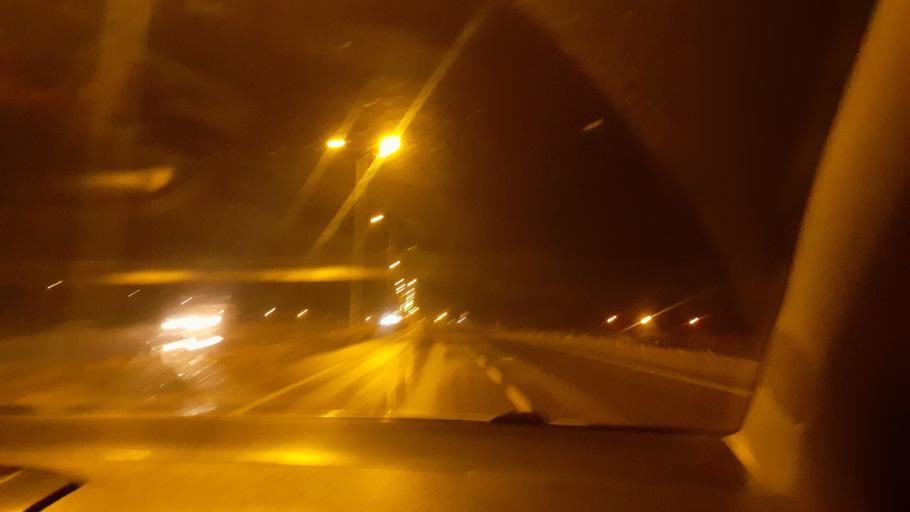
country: TR
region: Hatay
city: Aktepe
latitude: 36.7169
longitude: 36.5102
